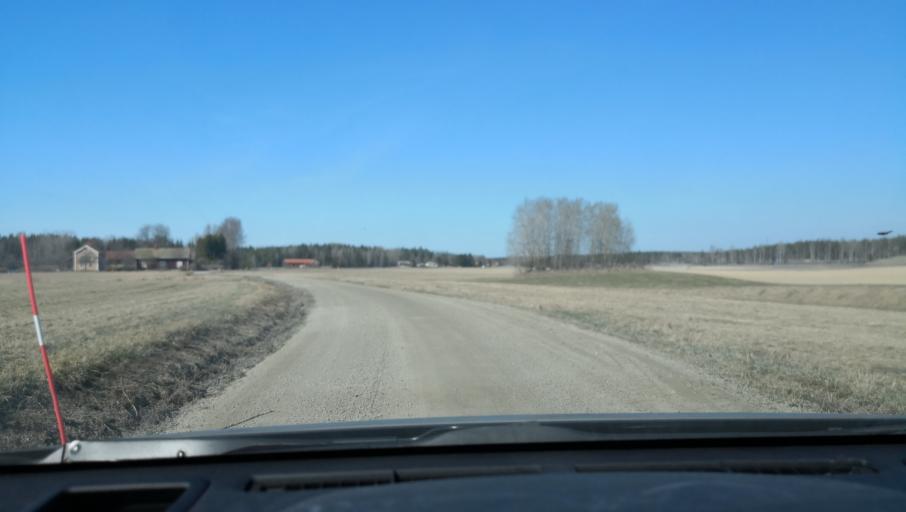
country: SE
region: Vaestmanland
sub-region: Sala Kommun
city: Sala
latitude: 59.8974
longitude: 16.5298
